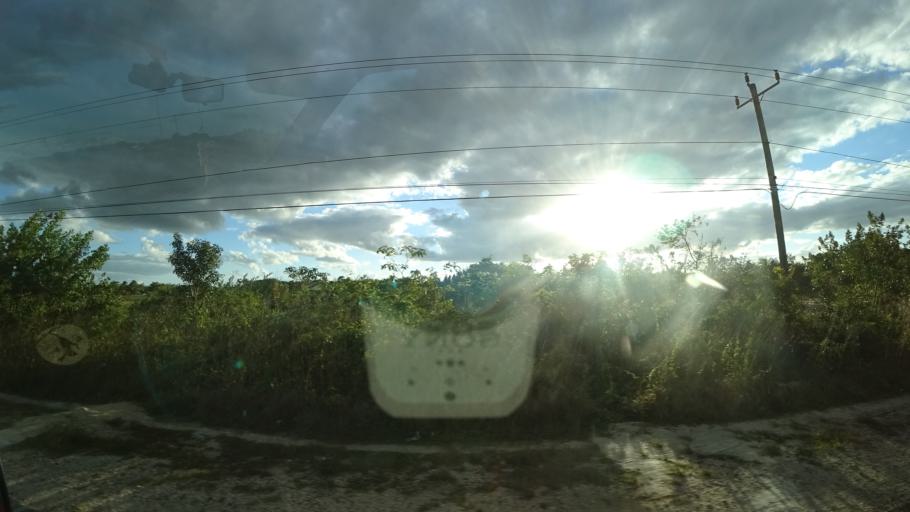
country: BZ
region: Belize
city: Belize City
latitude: 17.5609
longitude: -88.3217
